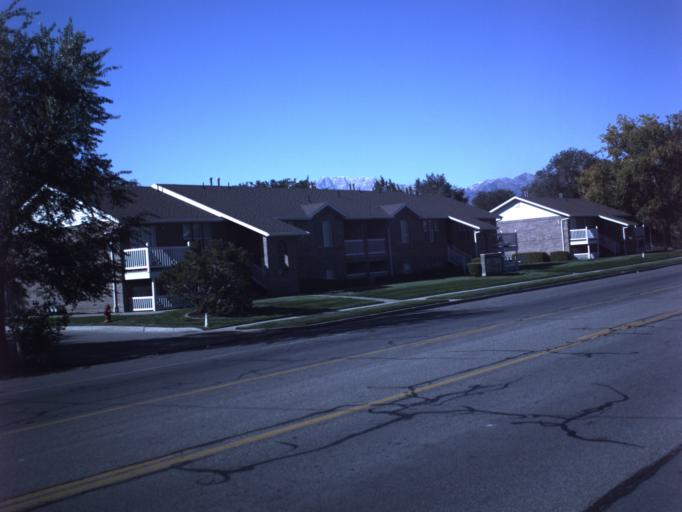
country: US
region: Utah
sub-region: Tooele County
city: Grantsville
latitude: 40.5998
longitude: -112.4479
